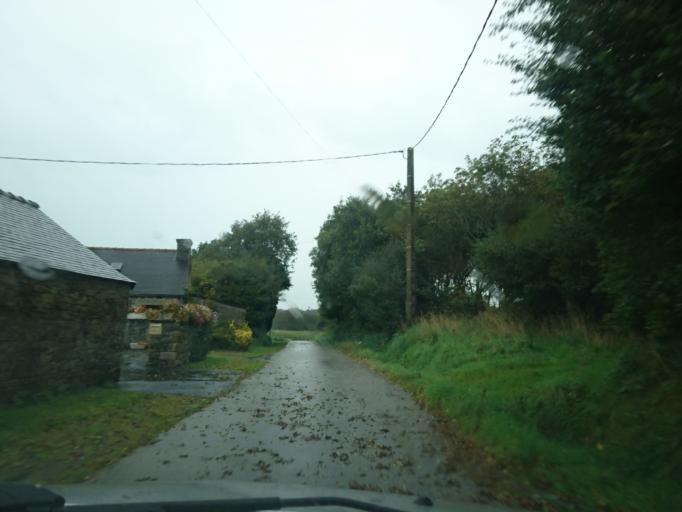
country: FR
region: Brittany
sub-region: Departement du Finistere
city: Kernilis
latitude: 48.5528
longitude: -4.3960
